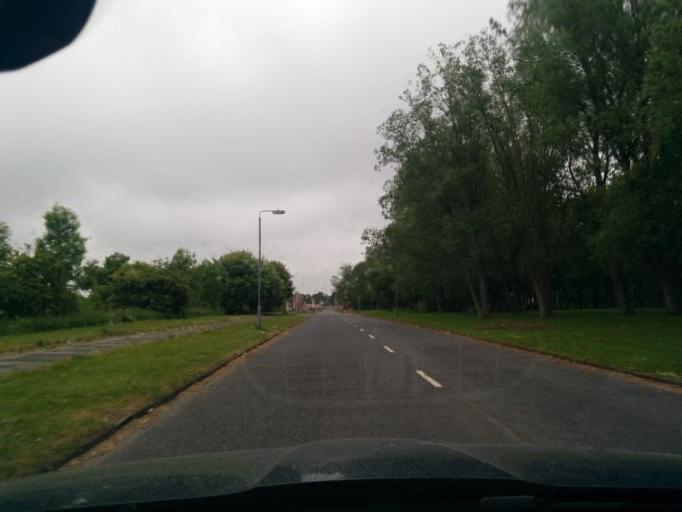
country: GB
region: England
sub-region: Northumberland
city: Cramlington
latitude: 55.0883
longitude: -1.6078
